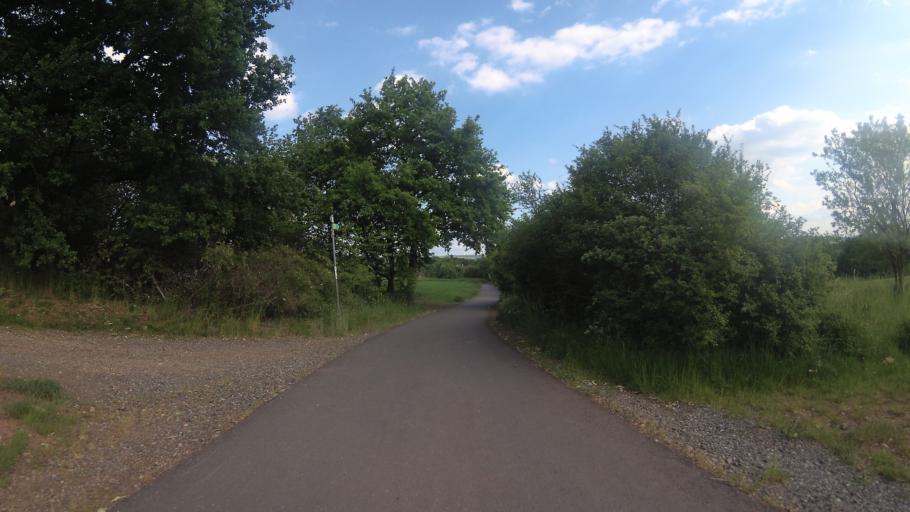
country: DE
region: Saarland
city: Namborn
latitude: 49.4941
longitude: 7.1543
